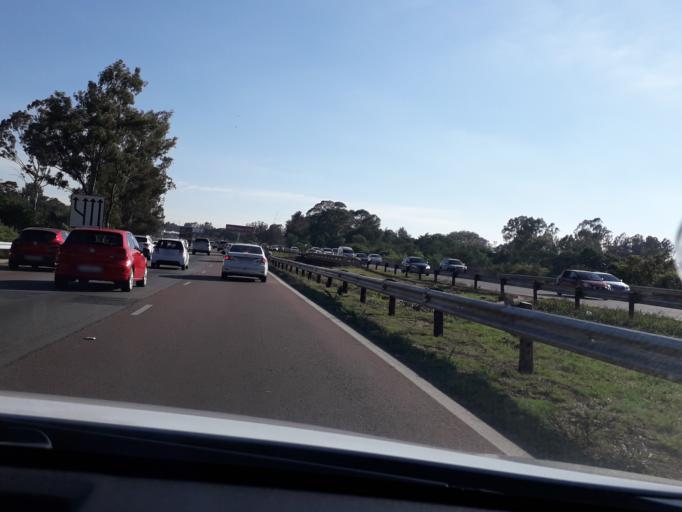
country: ZA
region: Gauteng
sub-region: City of Tshwane Metropolitan Municipality
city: Centurion
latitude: -25.8488
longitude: 28.1791
